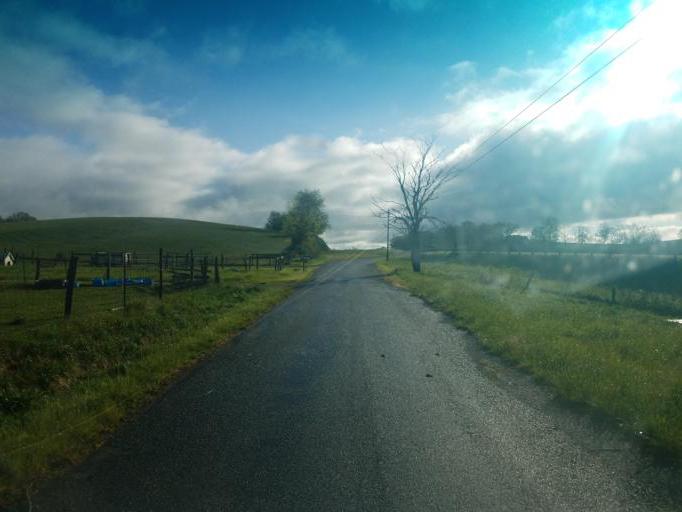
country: US
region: Virginia
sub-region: Washington County
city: Emory
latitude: 36.6917
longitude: -81.8057
